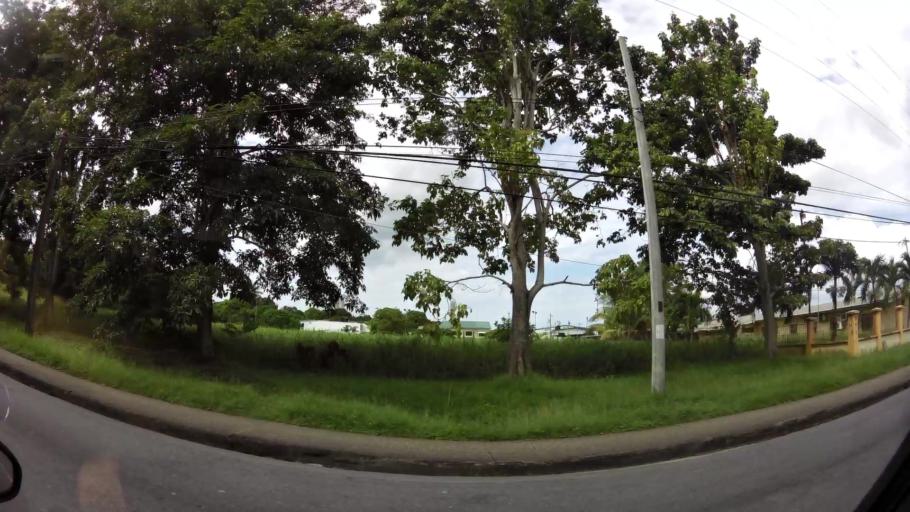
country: TT
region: Couva-Tabaquite-Talparo
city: Couva
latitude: 10.4166
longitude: -61.4707
